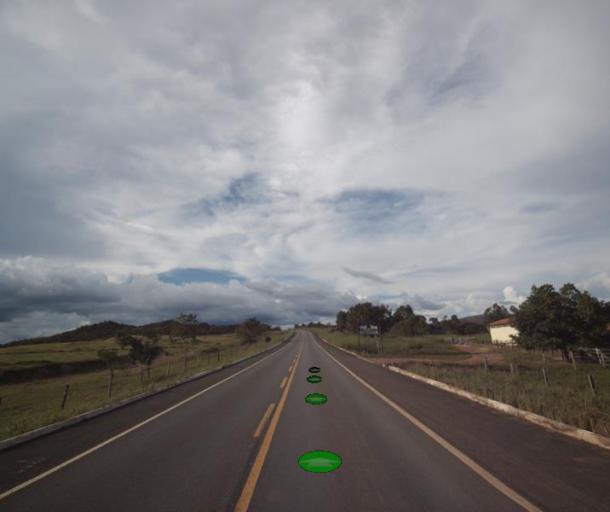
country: BR
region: Goias
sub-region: Niquelandia
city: Niquelandia
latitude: -14.6737
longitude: -48.5909
